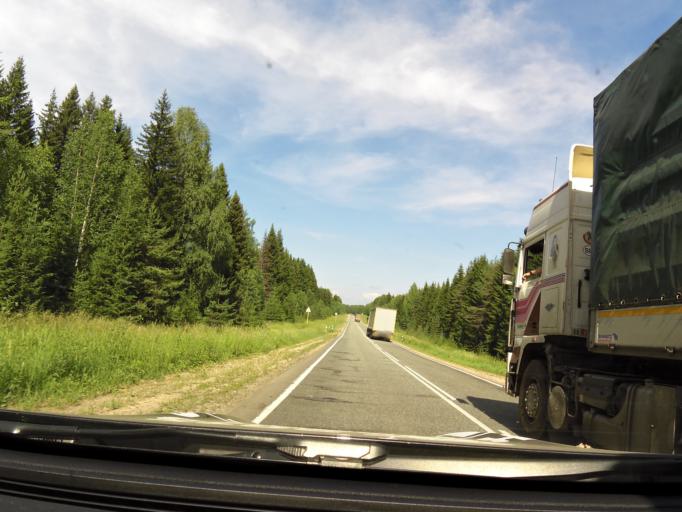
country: RU
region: Kirov
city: Belaya Kholunitsa
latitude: 58.8202
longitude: 50.6071
